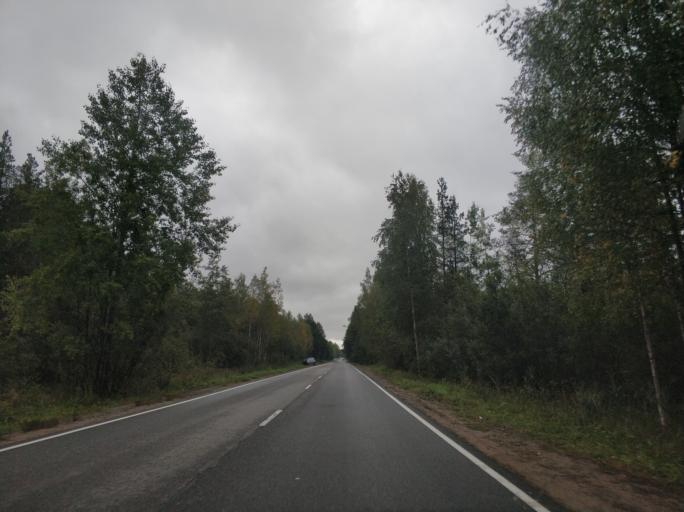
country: RU
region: Leningrad
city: Borisova Griva
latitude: 60.1437
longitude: 30.9473
